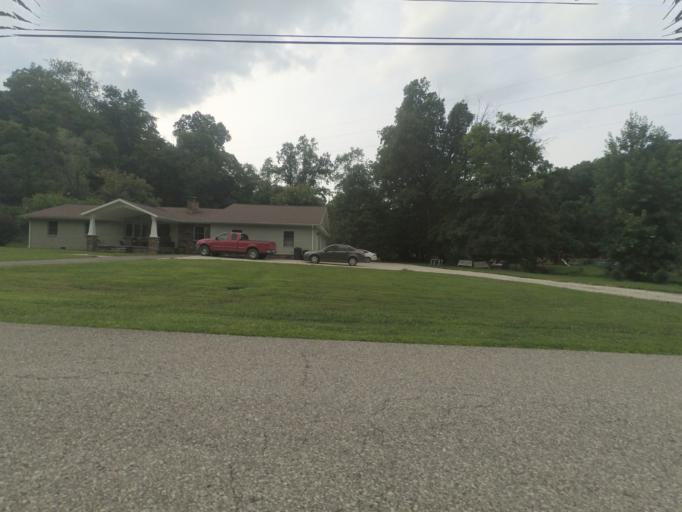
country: US
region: West Virginia
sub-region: Cabell County
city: Huntington
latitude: 38.3854
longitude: -82.4049
